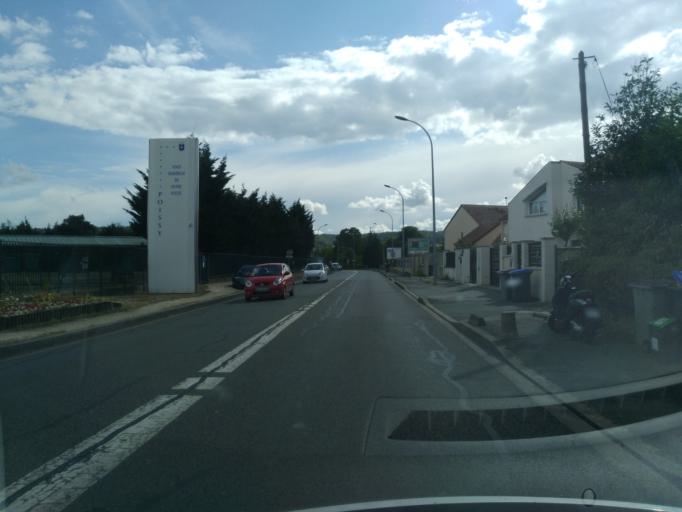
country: FR
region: Ile-de-France
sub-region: Departement des Yvelines
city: Chambourcy
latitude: 48.9177
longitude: 2.0258
